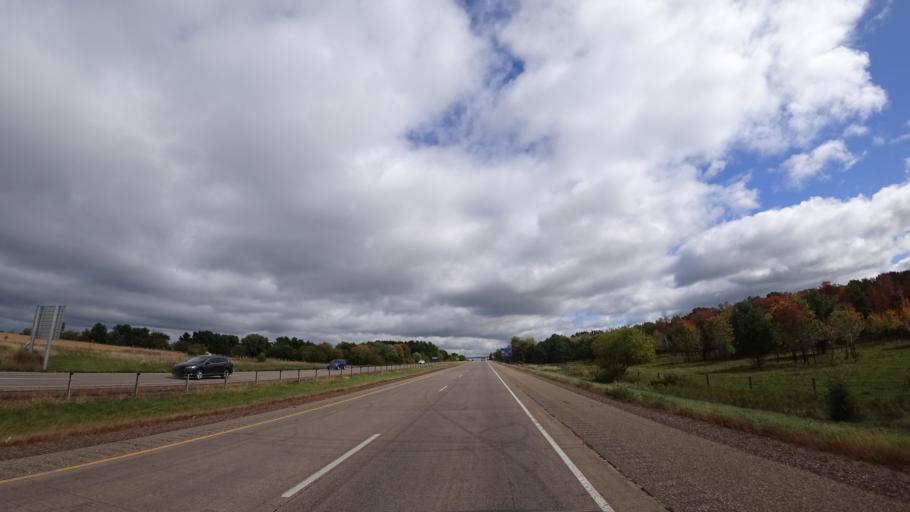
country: US
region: Wisconsin
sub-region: Chippewa County
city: Chippewa Falls
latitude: 44.9199
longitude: -91.3552
